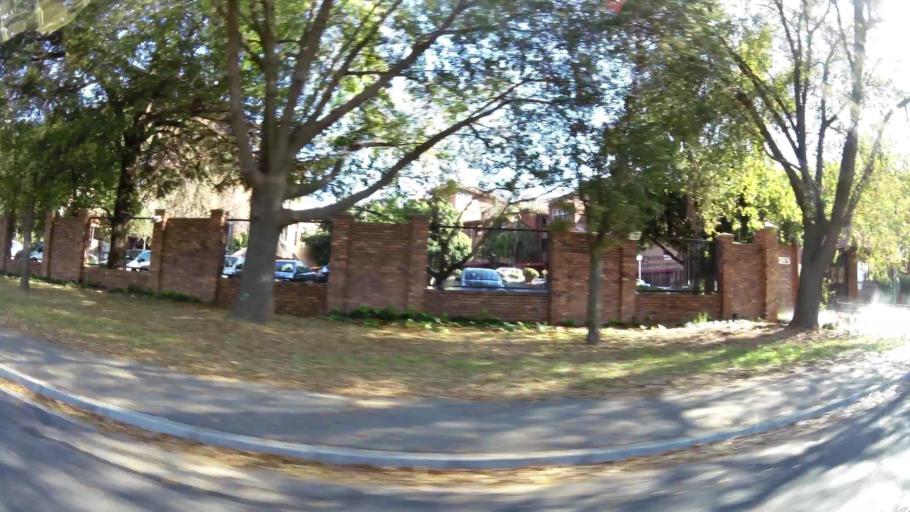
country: ZA
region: Gauteng
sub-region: City of Johannesburg Metropolitan Municipality
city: Modderfontein
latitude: -26.1436
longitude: 28.1102
